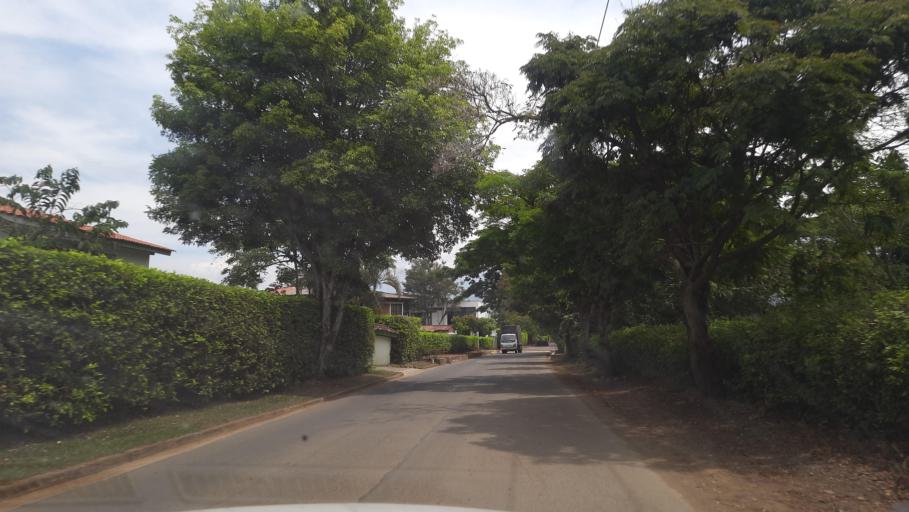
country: CO
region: Valle del Cauca
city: Jamundi
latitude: 3.2696
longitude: -76.5189
